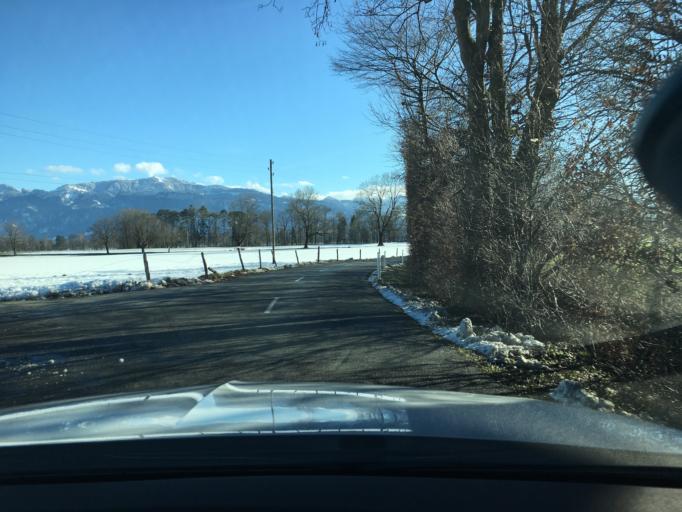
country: CH
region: Saint Gallen
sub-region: Wahlkreis Rheintal
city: Rebstein
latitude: 47.3818
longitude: 9.5854
